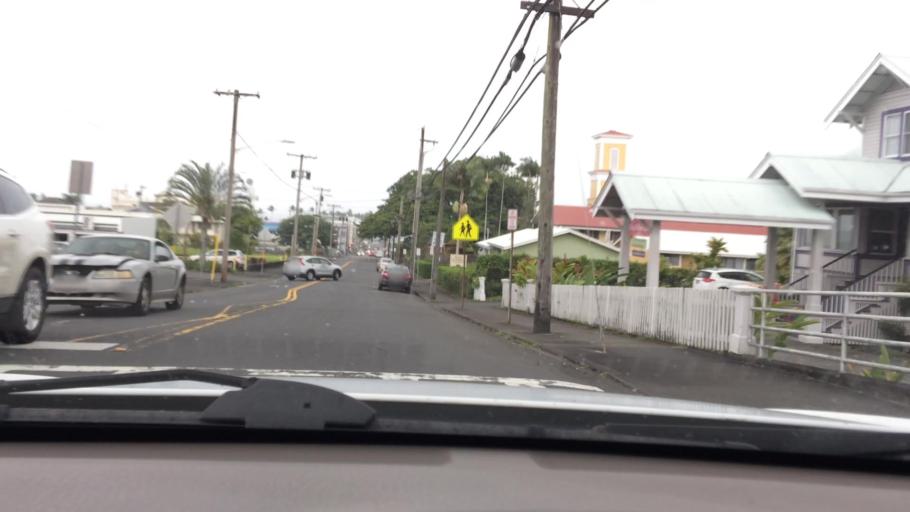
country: US
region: Hawaii
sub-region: Hawaii County
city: Hilo
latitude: 19.7222
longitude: -155.0903
